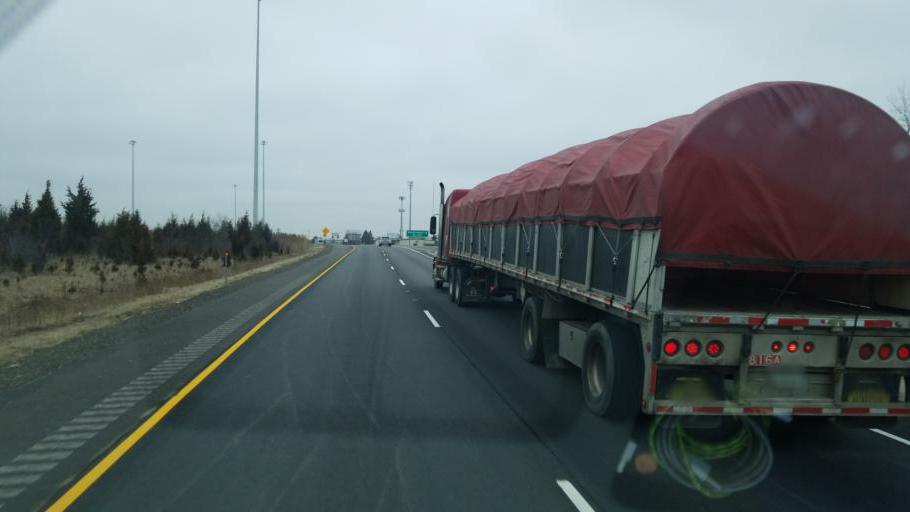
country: US
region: Illinois
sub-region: Lake County
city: Park City
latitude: 42.3510
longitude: -87.8930
